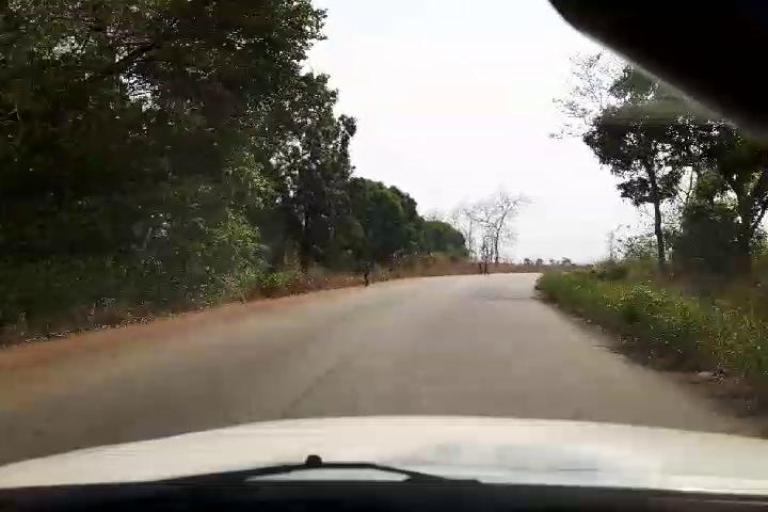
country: SL
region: Northern Province
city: Yonibana
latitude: 8.3799
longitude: -12.2017
